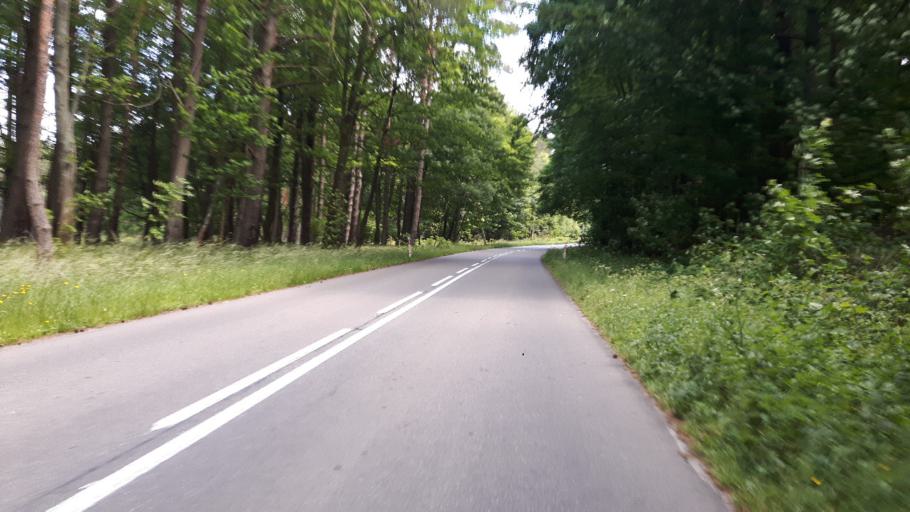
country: PL
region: Pomeranian Voivodeship
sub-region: Powiat leborski
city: Leba
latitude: 54.7450
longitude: 17.7167
